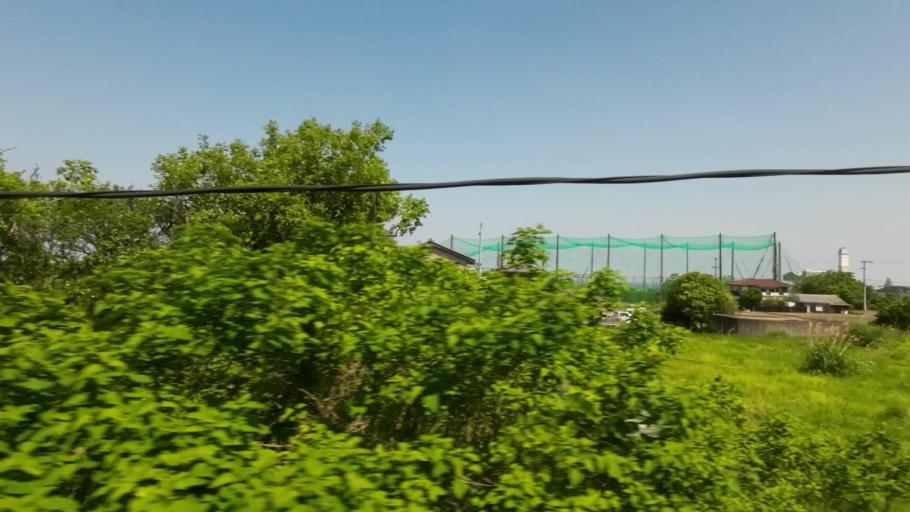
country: JP
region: Ehime
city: Kawanoecho
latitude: 33.9750
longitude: 133.5278
